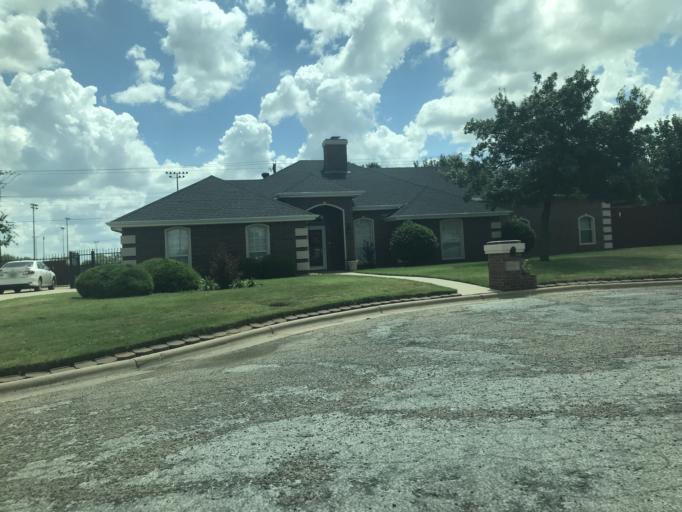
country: US
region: Texas
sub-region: Taylor County
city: Abilene
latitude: 32.4378
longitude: -99.6978
